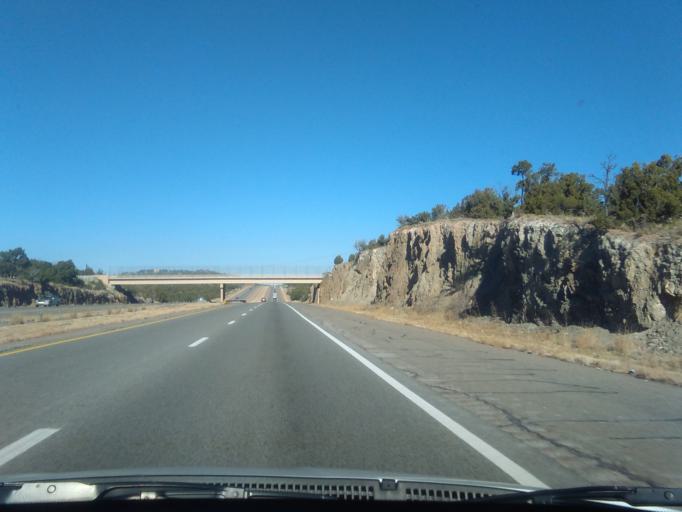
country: US
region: New Mexico
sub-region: Santa Fe County
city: Eldorado at Santa Fe
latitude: 35.6042
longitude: -105.9111
